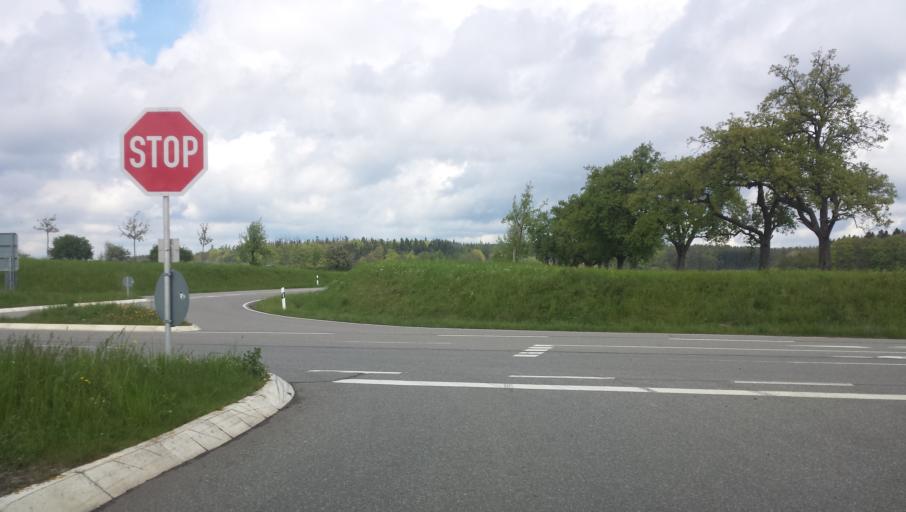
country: DE
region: Baden-Wuerttemberg
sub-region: Karlsruhe Region
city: Fahrenbach
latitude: 49.4587
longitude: 9.1013
